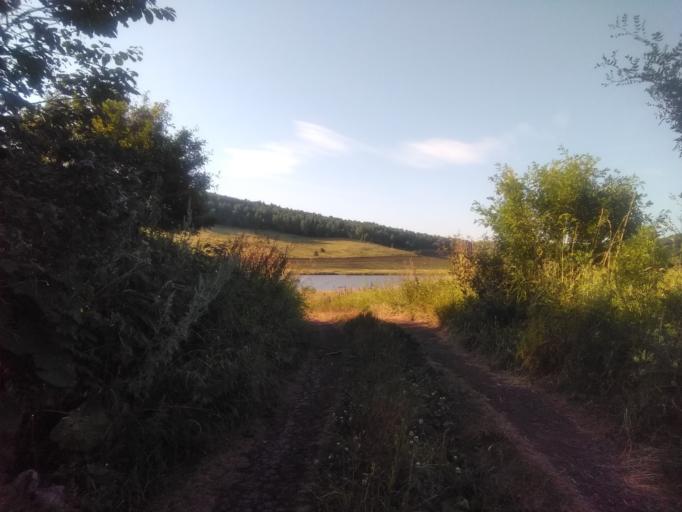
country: RU
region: Tatarstan
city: Russkiy Aktash
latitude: 54.8795
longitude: 52.0737
